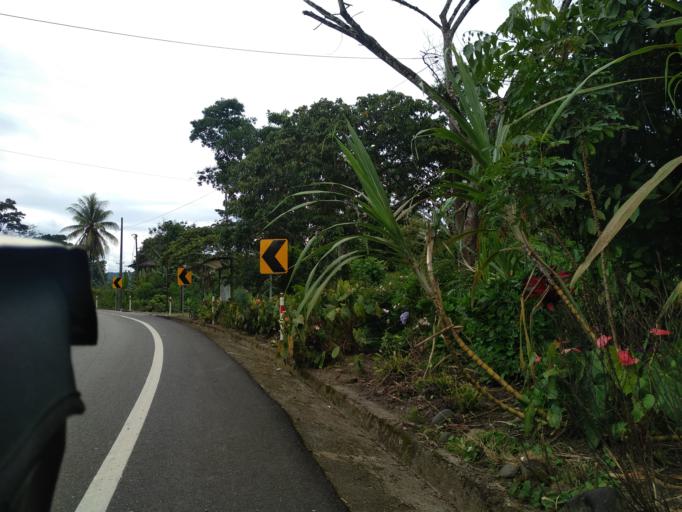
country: EC
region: Napo
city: Tena
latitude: -1.2440
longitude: -77.8773
